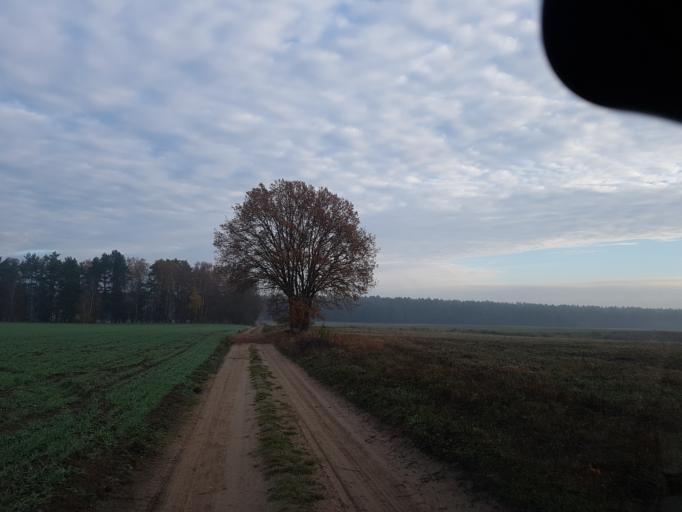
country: DE
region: Saxony-Anhalt
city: Abtsdorf
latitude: 51.9234
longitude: 12.7430
